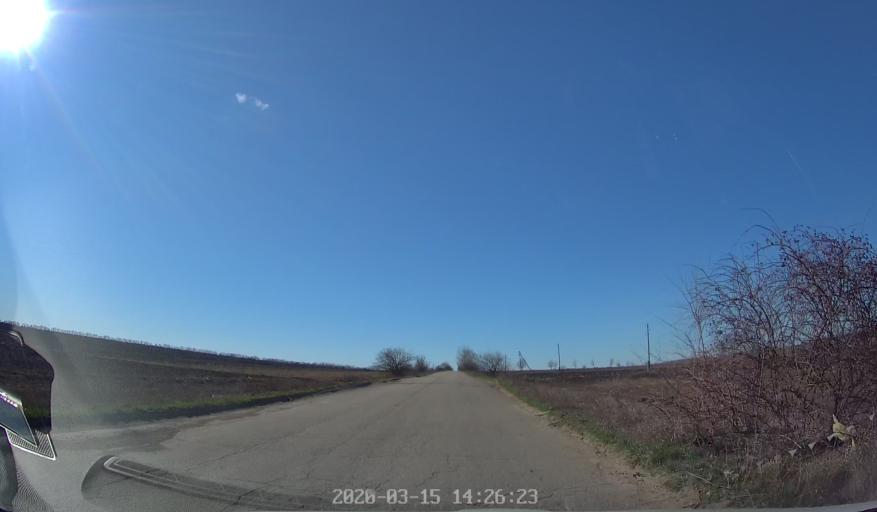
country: MD
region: Orhei
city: Orhei
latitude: 47.3427
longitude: 28.9075
